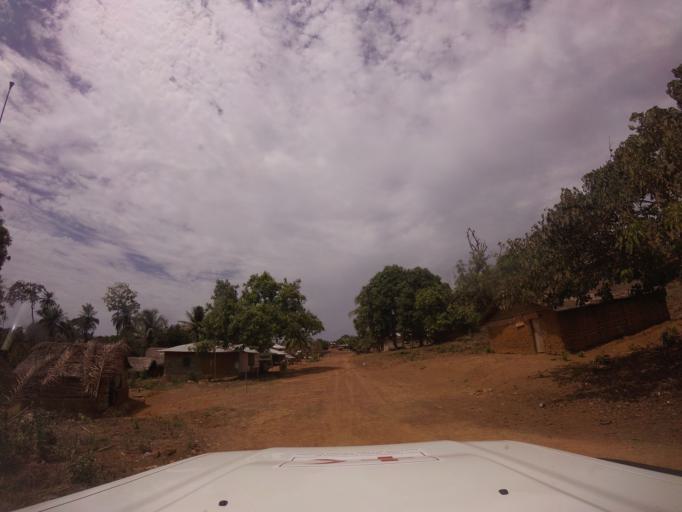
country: SL
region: Southern Province
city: Zimmi
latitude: 7.1616
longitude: -11.2431
